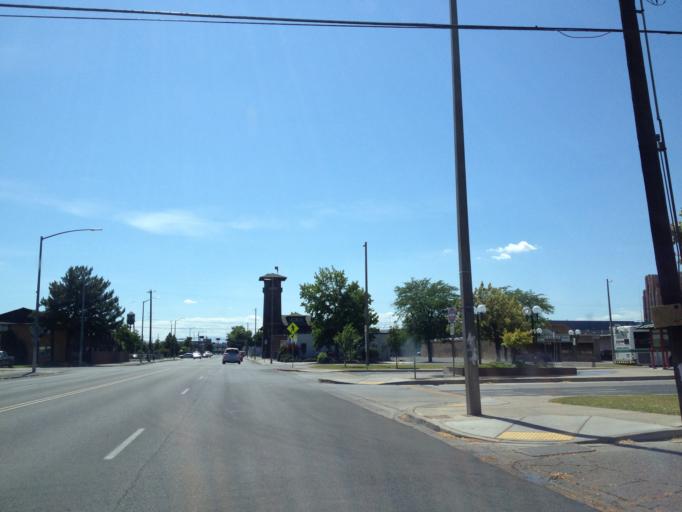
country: US
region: Washington
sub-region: Yakima County
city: Yakima
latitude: 46.6011
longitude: -120.4993
